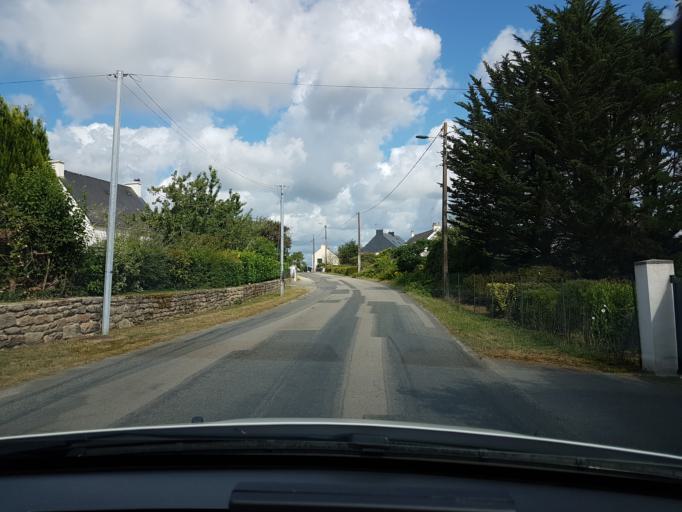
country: FR
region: Brittany
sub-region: Departement du Morbihan
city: Sainte-Helene
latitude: 47.7165
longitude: -3.1988
